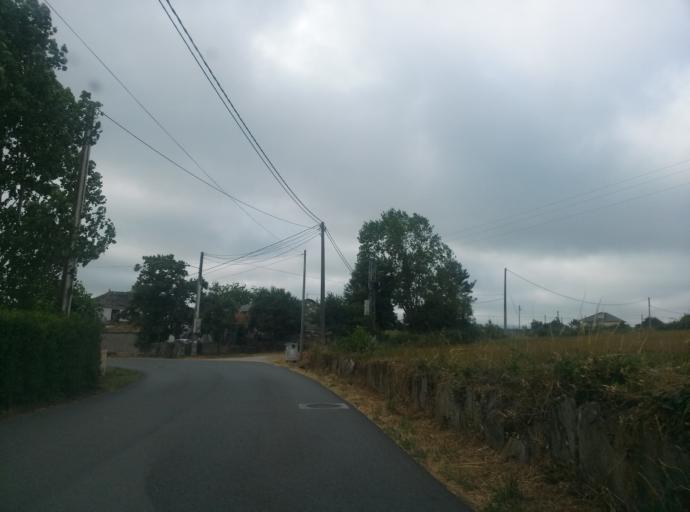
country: ES
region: Galicia
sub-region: Provincia de Lugo
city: Lugo
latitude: 43.0574
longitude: -7.5662
